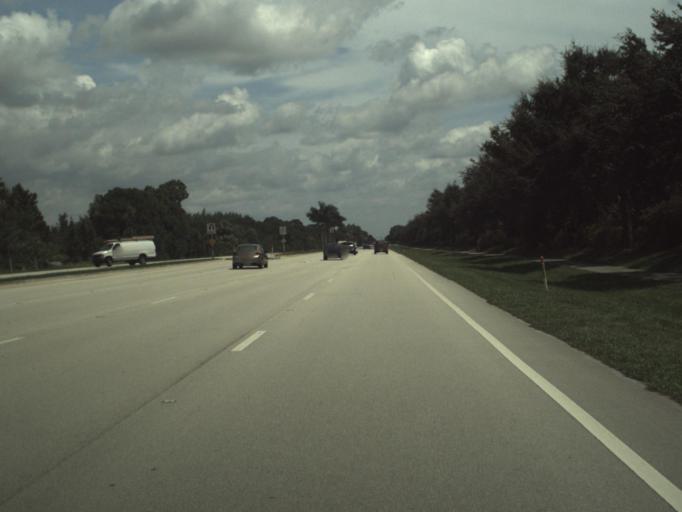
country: US
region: Florida
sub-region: Palm Beach County
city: Juno Beach
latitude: 26.8895
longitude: -80.0949
